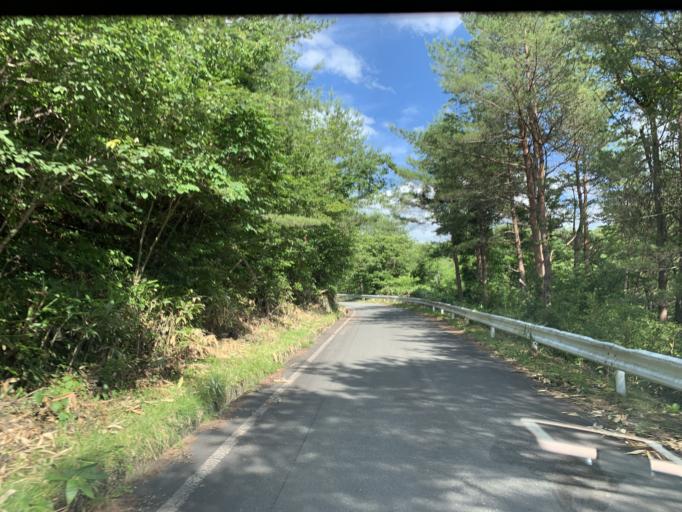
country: JP
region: Iwate
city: Ichinoseki
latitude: 38.9264
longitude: 140.9253
